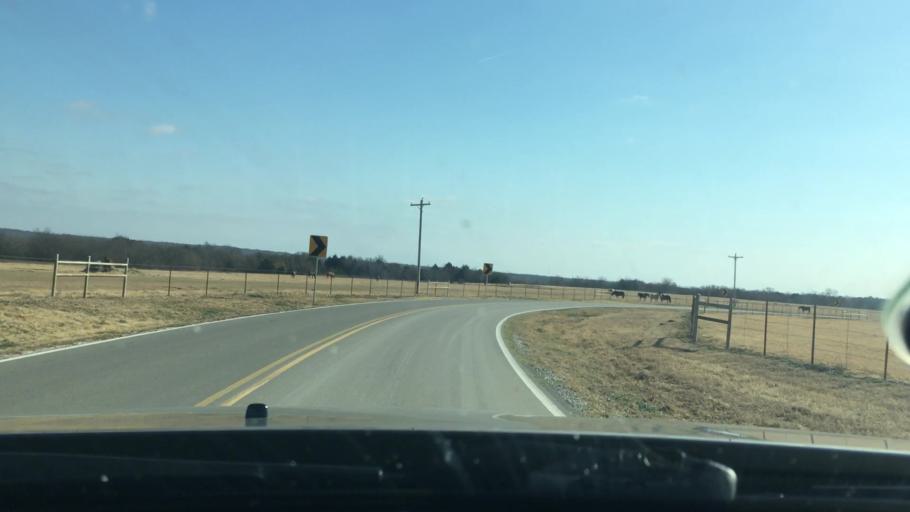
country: US
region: Oklahoma
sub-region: Marshall County
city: Oakland
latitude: 34.0251
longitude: -96.9315
